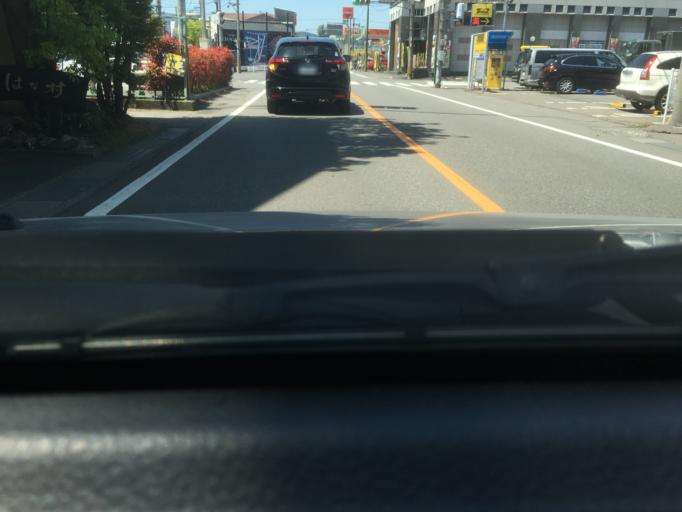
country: JP
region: Oita
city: Beppu
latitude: 33.2669
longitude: 131.3613
